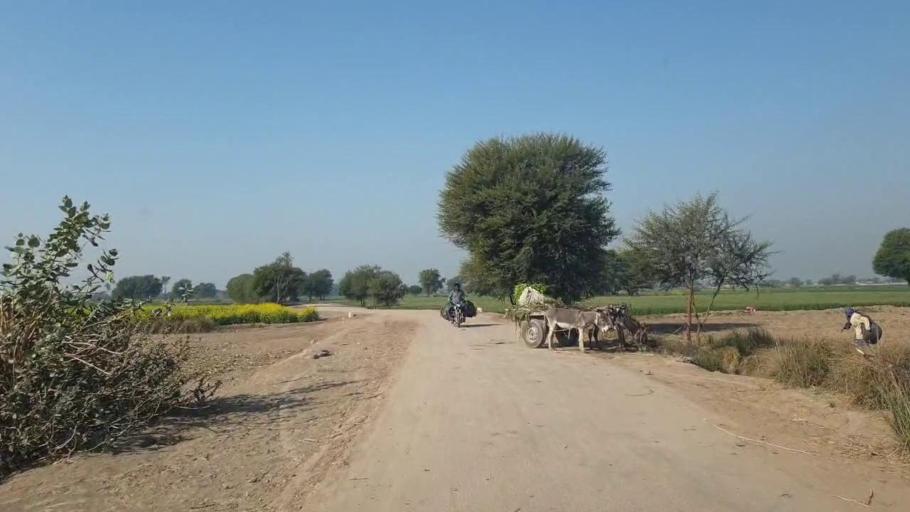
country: PK
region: Sindh
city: Shahpur Chakar
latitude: 26.0812
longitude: 68.5879
